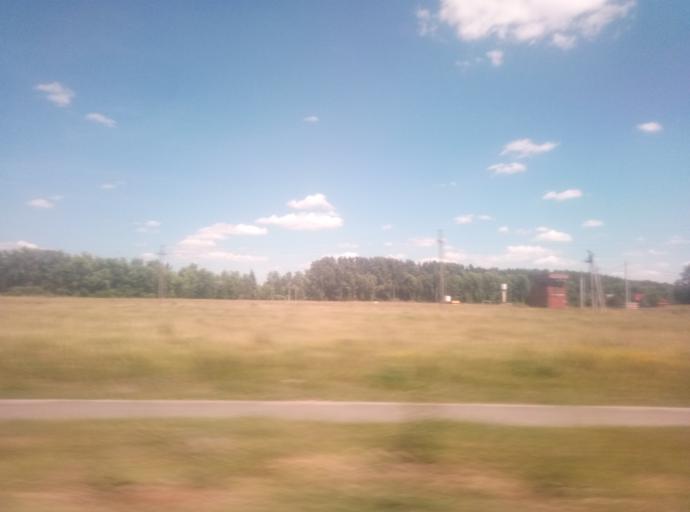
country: RU
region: Tula
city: Kireyevsk
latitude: 54.0181
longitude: 37.9106
